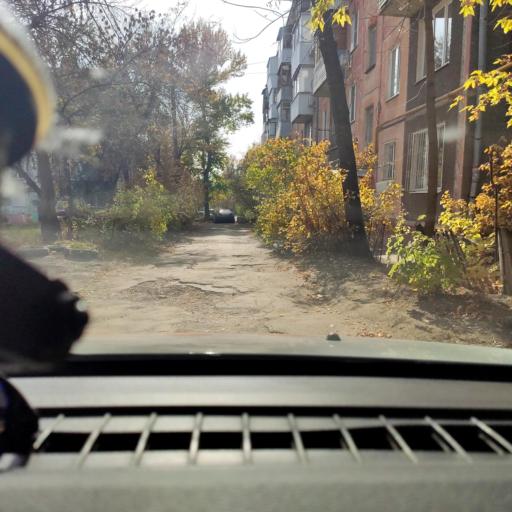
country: RU
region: Samara
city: Samara
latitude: 53.2021
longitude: 50.2082
